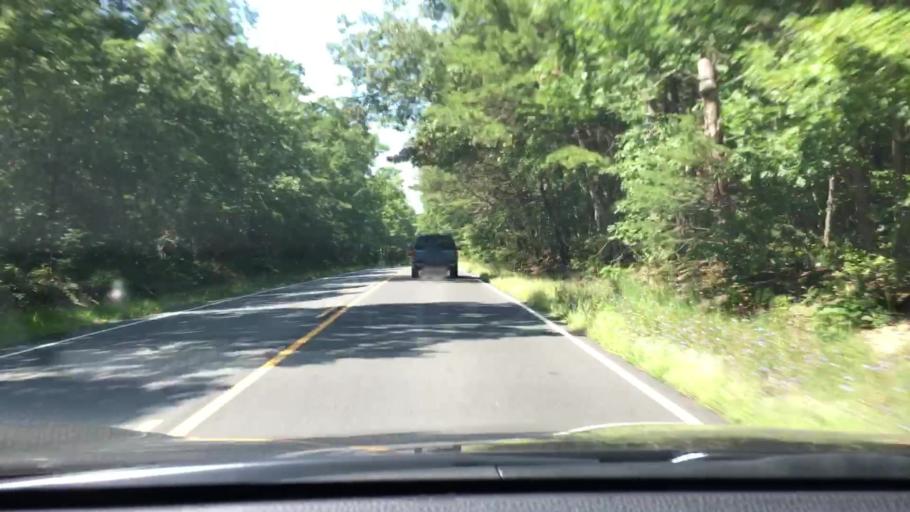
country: US
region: New Jersey
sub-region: Cape May County
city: Woodbine
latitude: 39.2597
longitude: -74.9049
